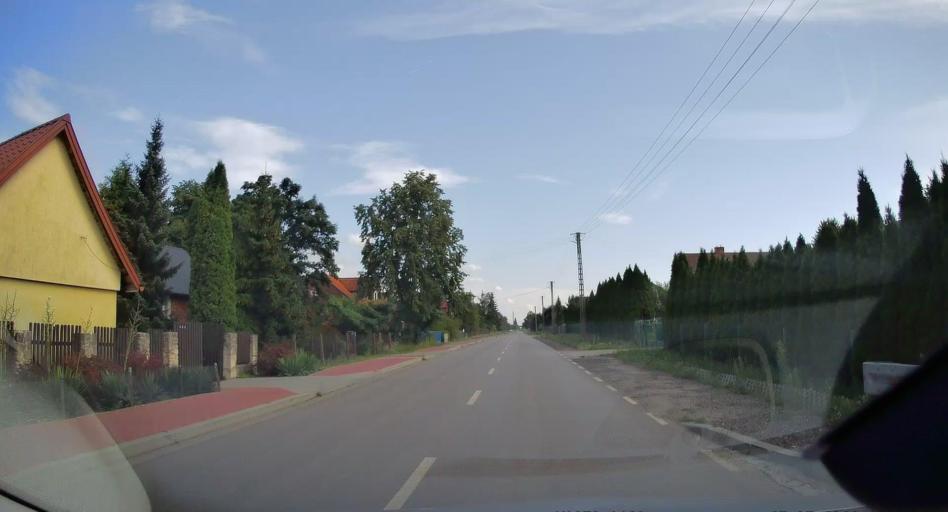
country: PL
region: Lodz Voivodeship
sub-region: Powiat opoczynski
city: Bialaczow
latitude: 51.2992
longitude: 20.3630
